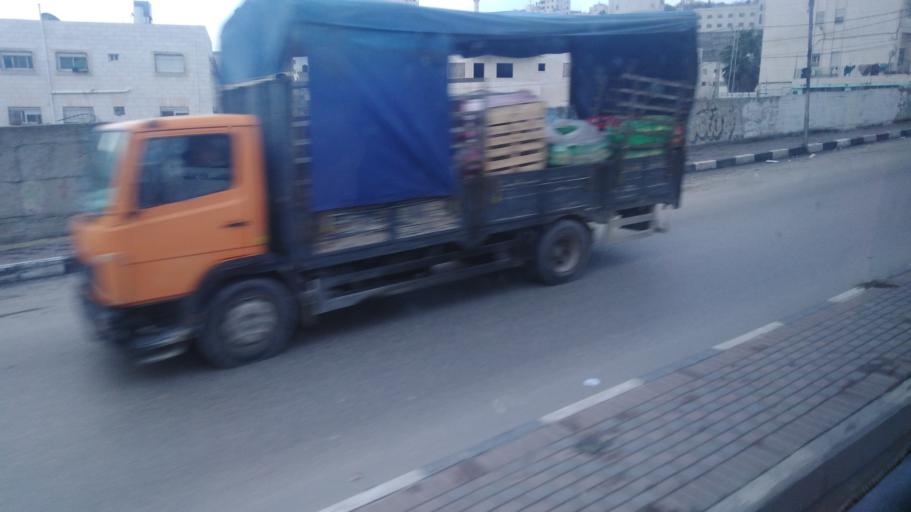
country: PS
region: West Bank
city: Hebron
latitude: 31.5306
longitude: 35.0891
